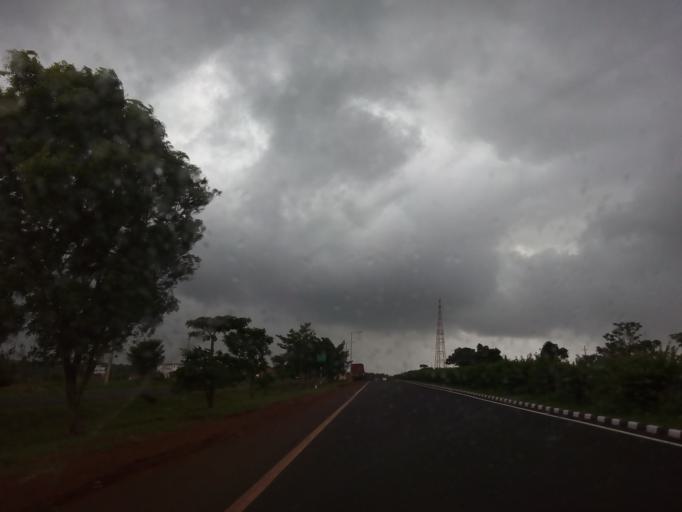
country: IN
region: Karnataka
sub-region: Belgaum
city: Belgaum
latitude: 16.0216
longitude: 74.5214
